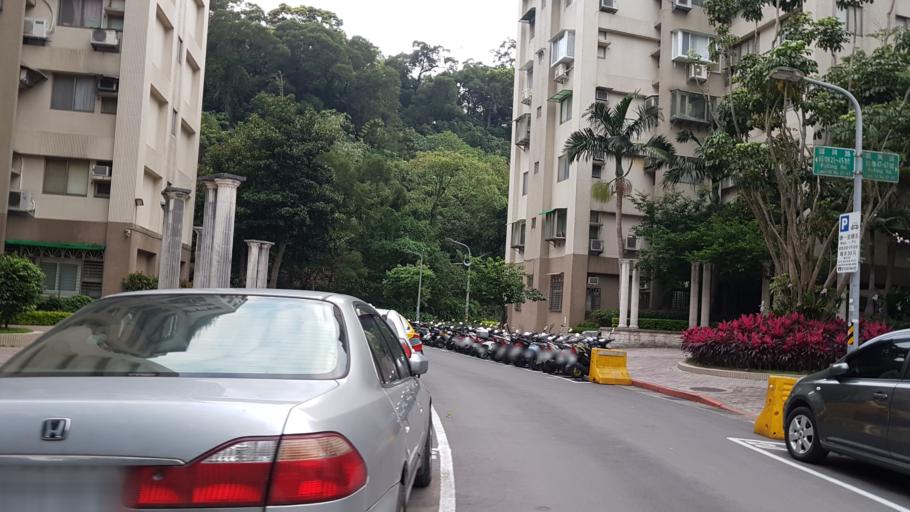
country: TW
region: Taipei
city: Taipei
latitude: 25.0055
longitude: 121.5474
